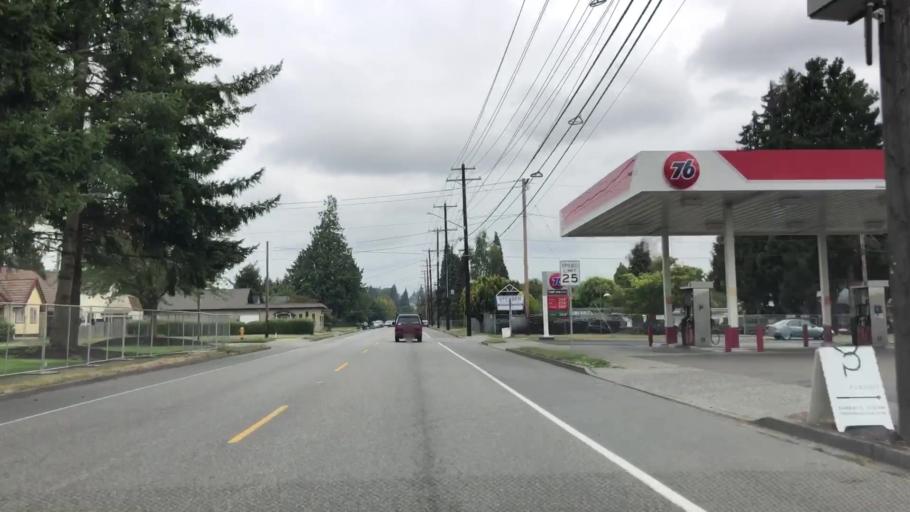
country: US
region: Washington
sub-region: Snohomish County
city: Snohomish
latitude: 47.9136
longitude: -122.0861
